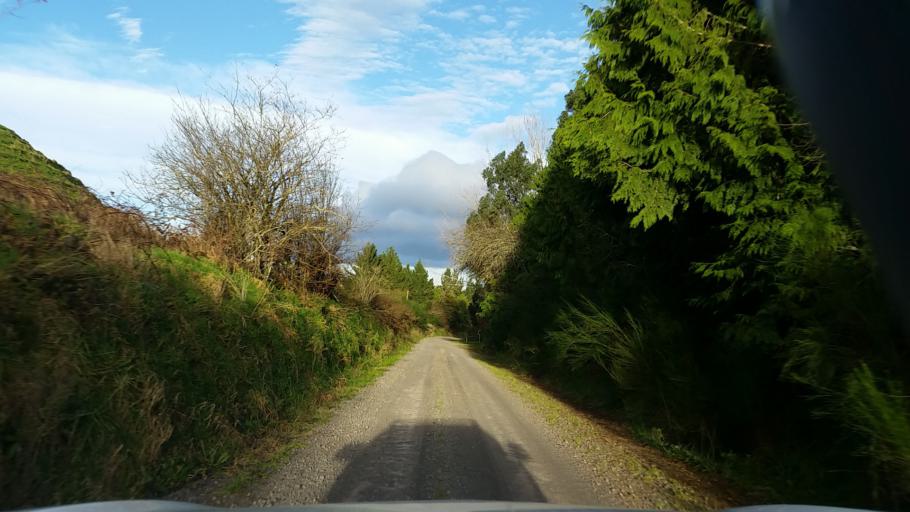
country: NZ
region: Bay of Plenty
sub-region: Rotorua District
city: Rotorua
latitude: -38.3001
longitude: 176.2743
